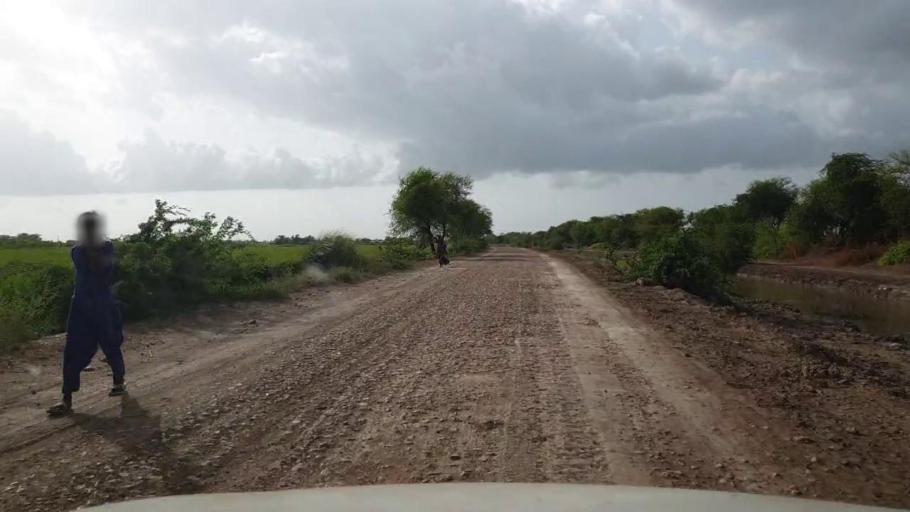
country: PK
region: Sindh
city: Kario
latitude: 24.7859
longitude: 68.5845
